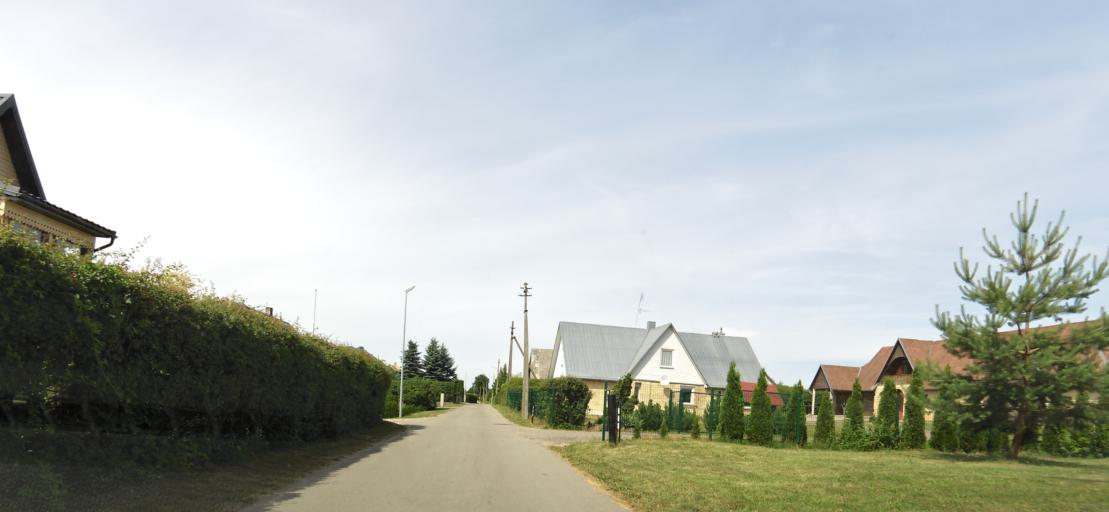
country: LT
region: Panevezys
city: Pasvalys
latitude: 55.9330
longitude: 24.3467
